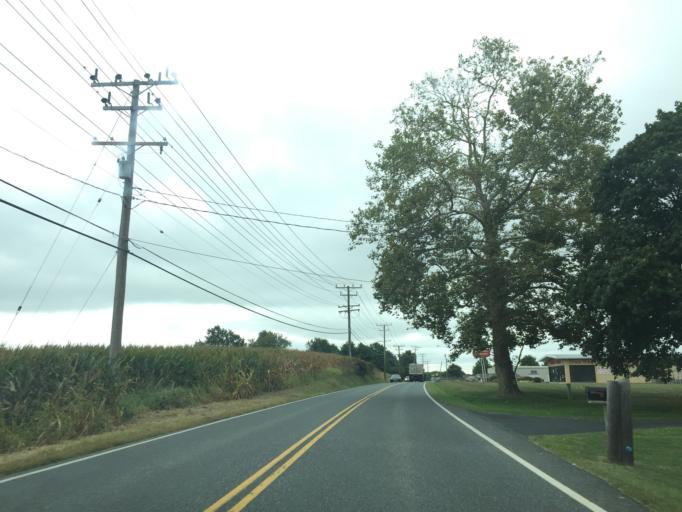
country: US
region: Maryland
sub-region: Harford County
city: Bel Air North
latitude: 39.5811
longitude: -76.3749
